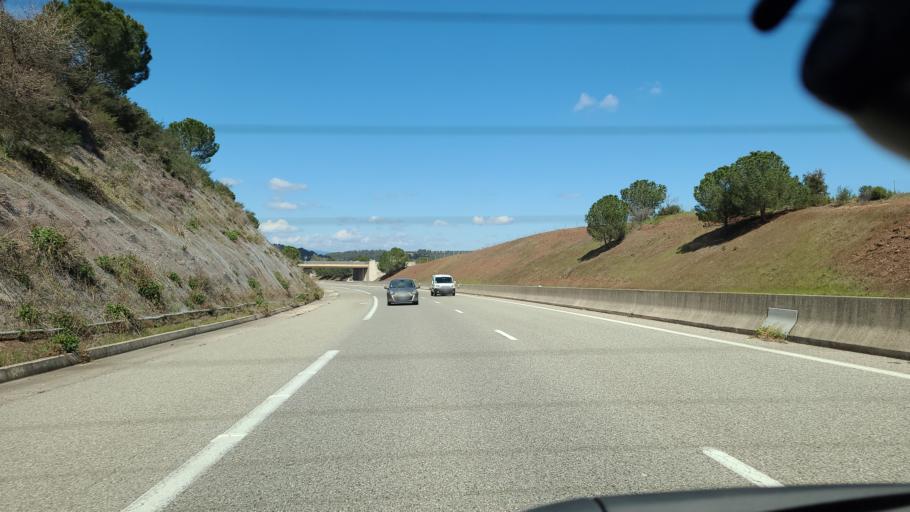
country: FR
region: Provence-Alpes-Cote d'Azur
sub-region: Departement du Var
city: Le Cannet-des-Maures
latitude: 43.3842
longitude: 6.3591
